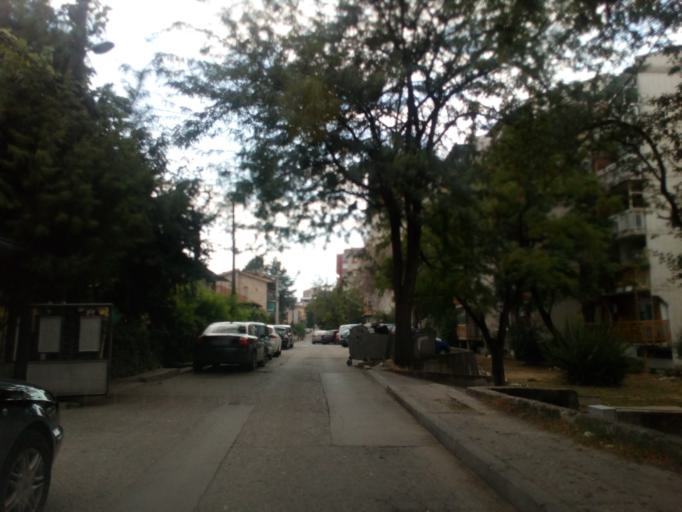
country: MK
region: Veles
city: Veles
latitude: 41.7165
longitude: 21.7741
